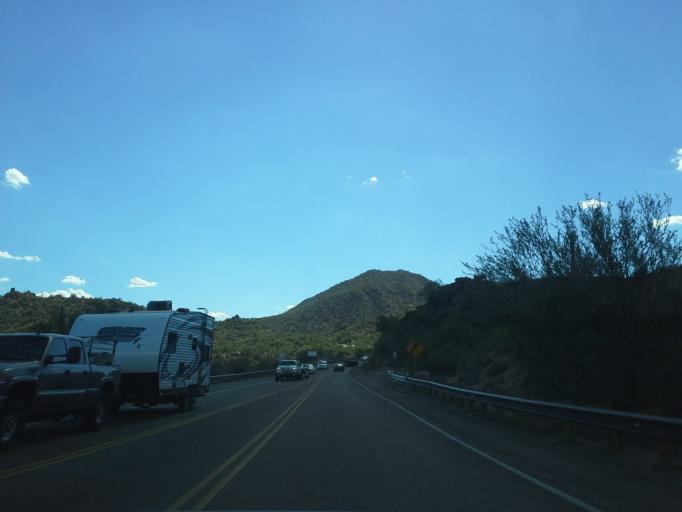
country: US
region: Arizona
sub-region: Pinal County
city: Apache Junction
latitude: 33.5752
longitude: -111.5419
